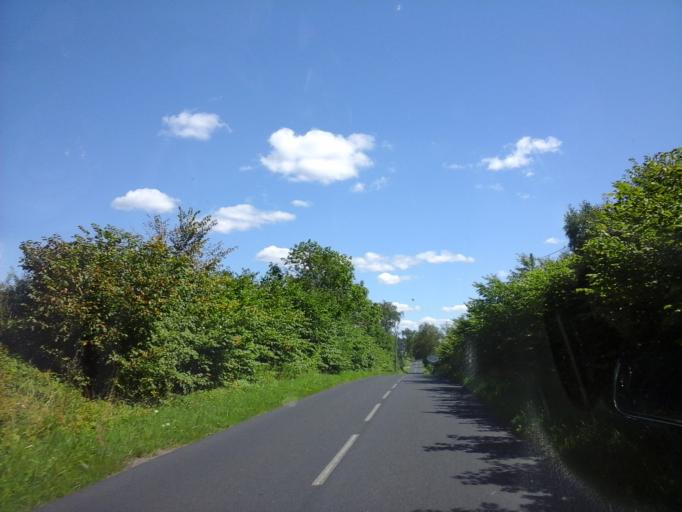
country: PL
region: West Pomeranian Voivodeship
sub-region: Powiat choszczenski
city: Drawno
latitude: 53.2410
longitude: 15.7354
